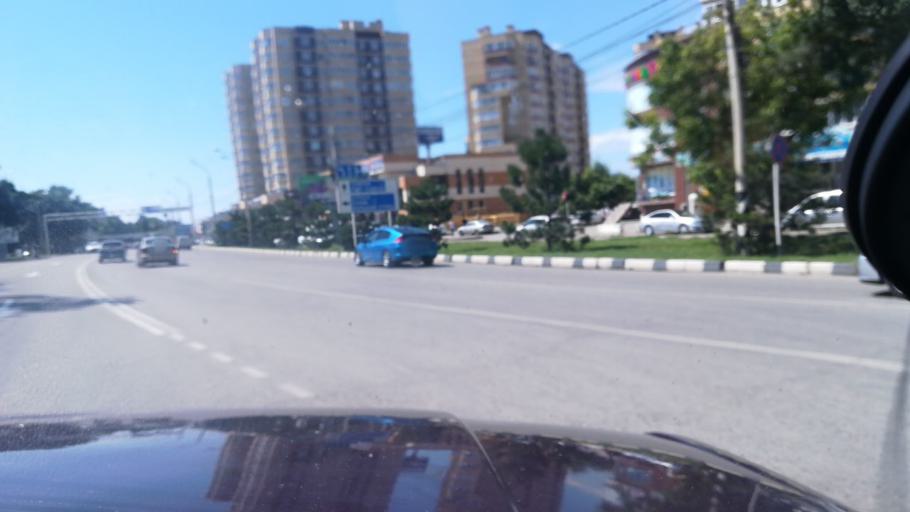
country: RU
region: Krasnodarskiy
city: Anapa
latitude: 44.8993
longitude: 37.3436
